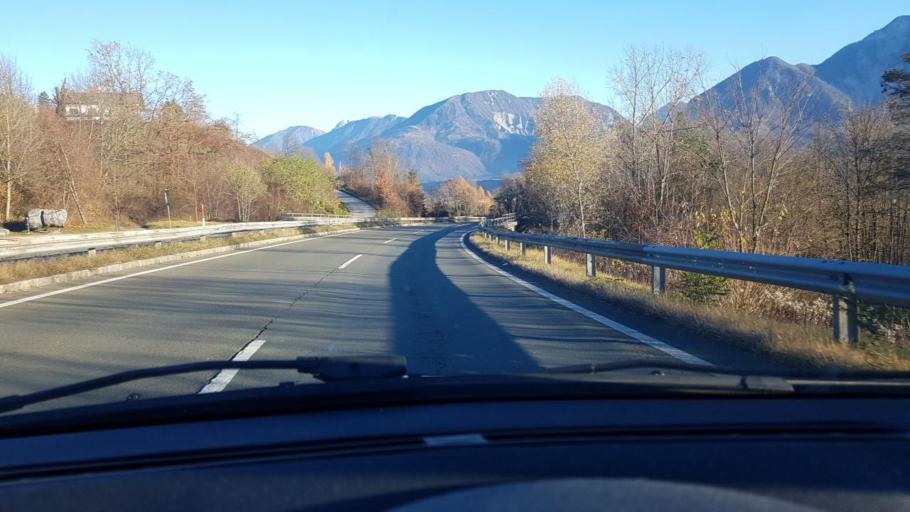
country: AT
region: Carinthia
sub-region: Politischer Bezirk Klagenfurt Land
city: Kottmannsdorf
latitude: 46.5453
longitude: 14.2507
